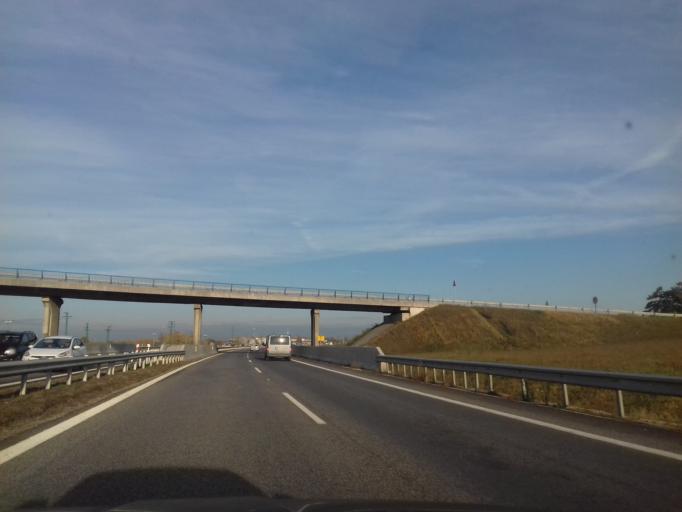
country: SK
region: Trnavsky
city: Sladkovicovo
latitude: 48.3004
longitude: 17.6601
